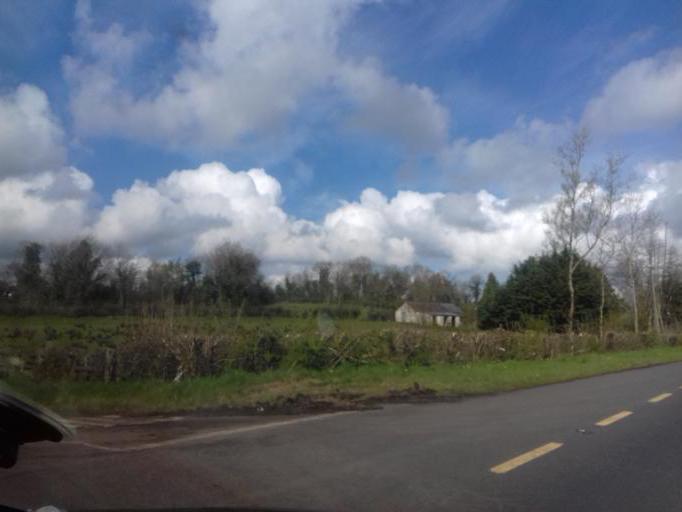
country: IE
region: Ulster
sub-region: An Cabhan
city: Belturbet
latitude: 54.1063
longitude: -7.4685
